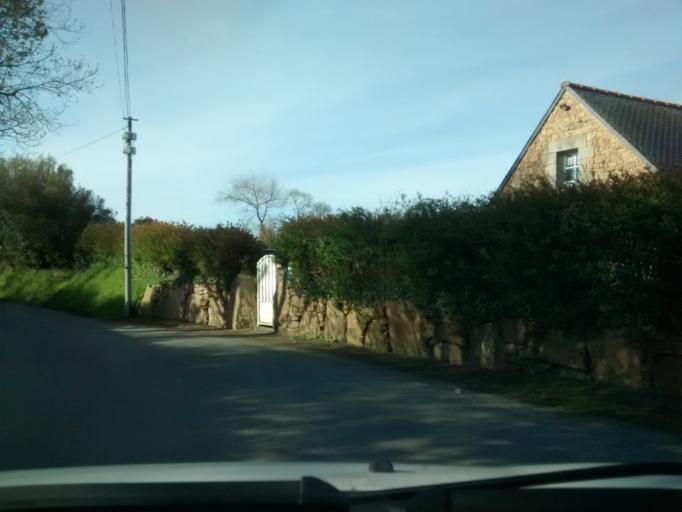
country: FR
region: Brittany
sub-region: Departement des Cotes-d'Armor
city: Penvenan
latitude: 48.8061
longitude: -3.3020
